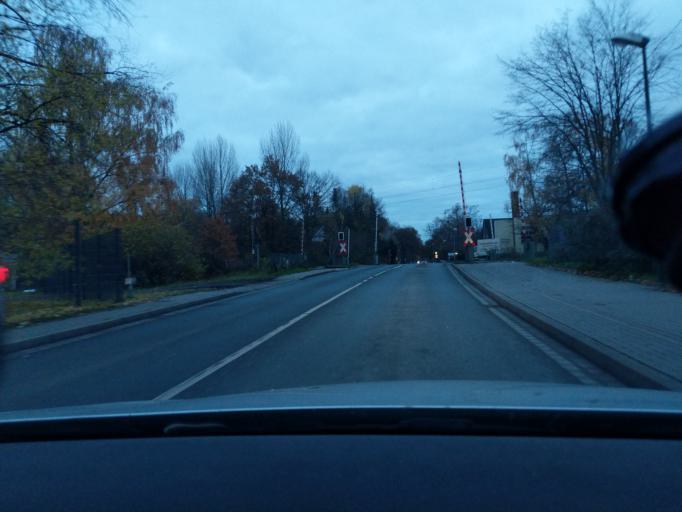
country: DE
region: North Rhine-Westphalia
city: Lunen
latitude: 51.6134
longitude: 7.4774
